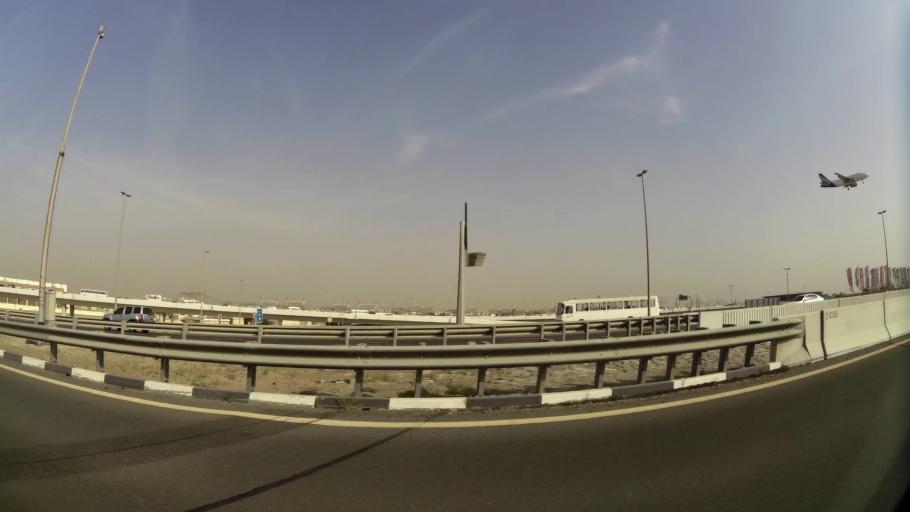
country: AE
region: Ash Shariqah
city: Sharjah
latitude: 25.2334
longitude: 55.4042
